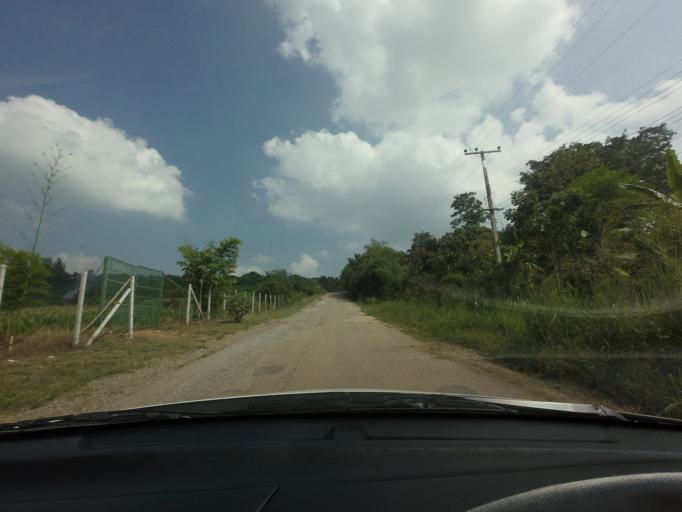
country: TH
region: Nakhon Ratchasima
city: Pak Chong
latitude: 14.5432
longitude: 101.5939
